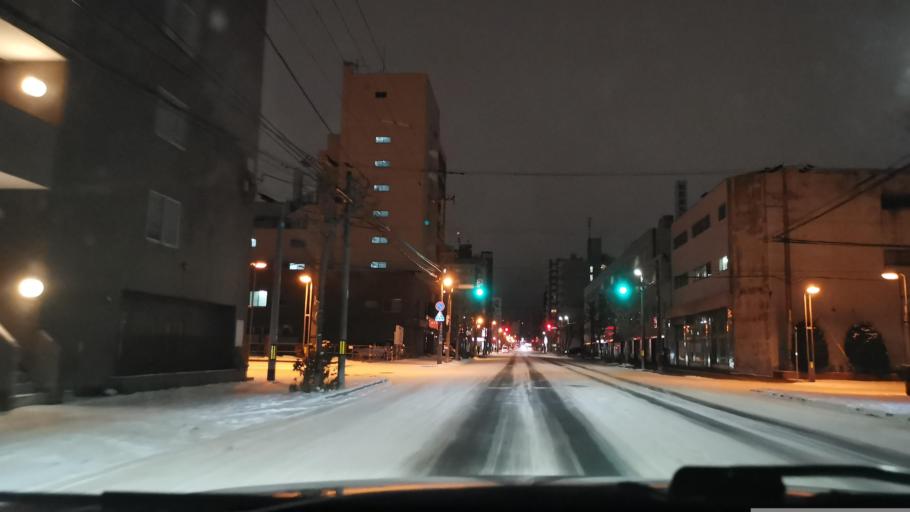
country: JP
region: Hokkaido
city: Sapporo
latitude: 43.0599
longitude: 141.3745
